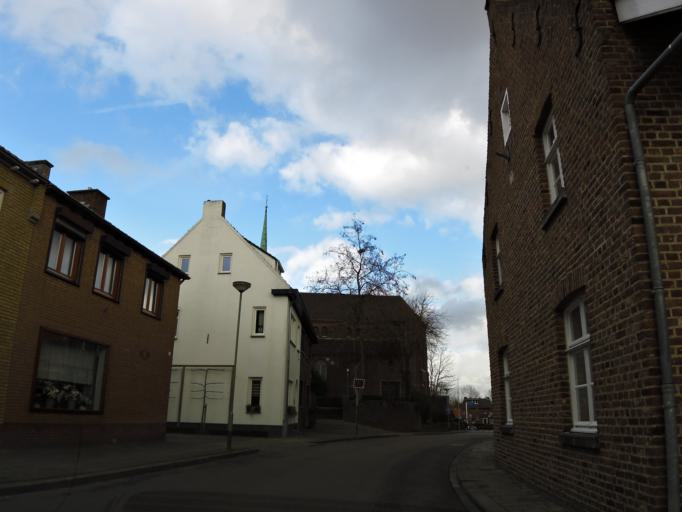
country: NL
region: Limburg
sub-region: Gemeente Stein
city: Berg
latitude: 51.0039
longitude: 5.7695
